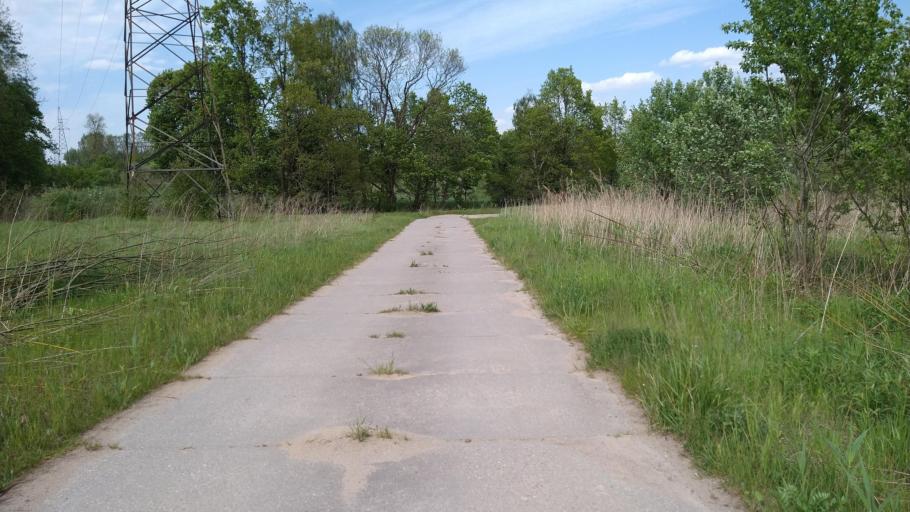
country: PL
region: Warmian-Masurian Voivodeship
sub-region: Powiat olsztynski
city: Olsztyn
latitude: 53.7912
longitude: 20.5472
